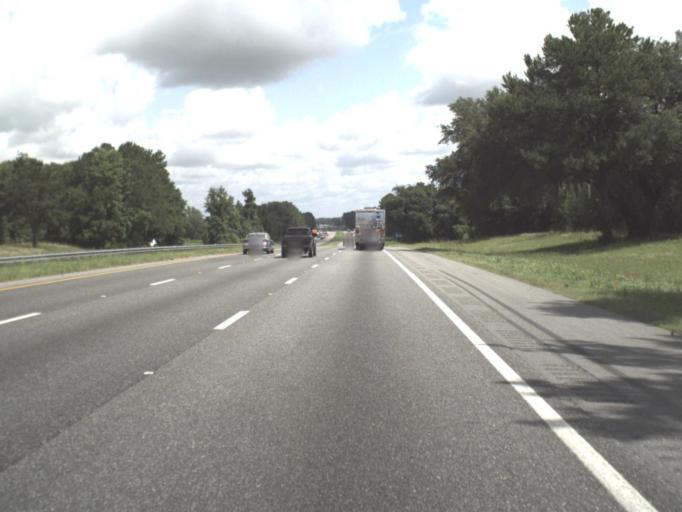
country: US
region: Florida
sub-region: Alachua County
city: High Springs
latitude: 29.9582
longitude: -82.5707
